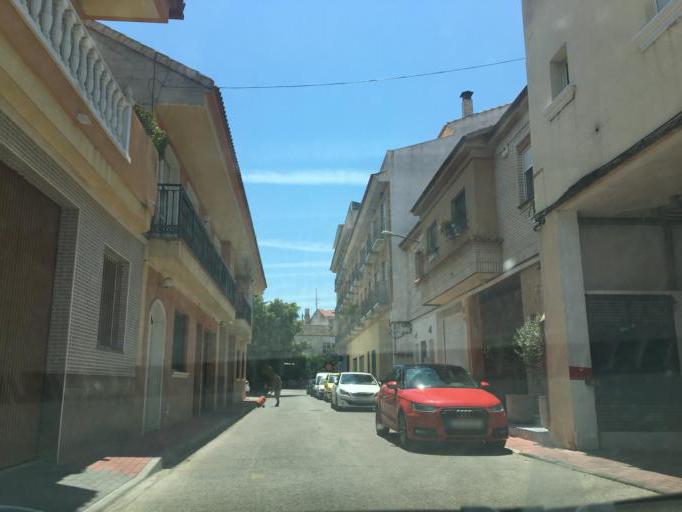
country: ES
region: Murcia
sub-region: Murcia
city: Santomera
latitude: 38.0162
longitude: -1.0535
